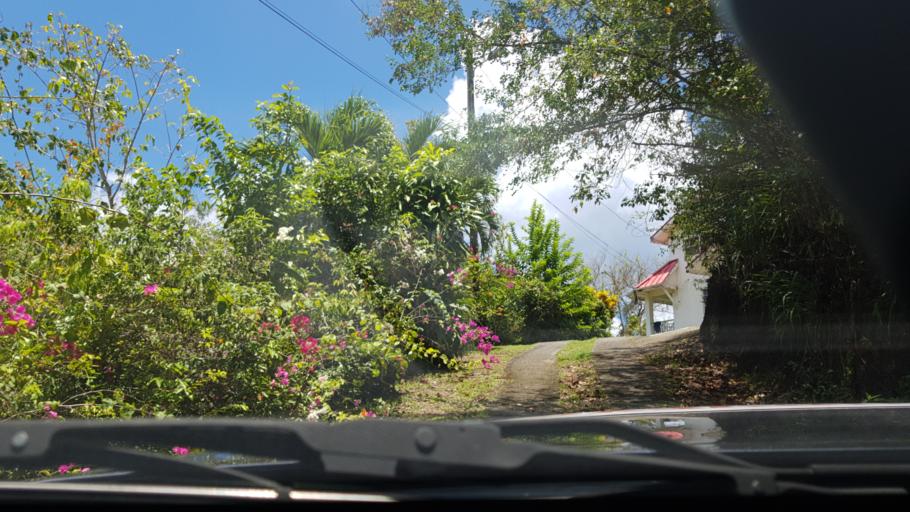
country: LC
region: Anse-la-Raye
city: Anse La Raye
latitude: 13.9405
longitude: -61.0401
